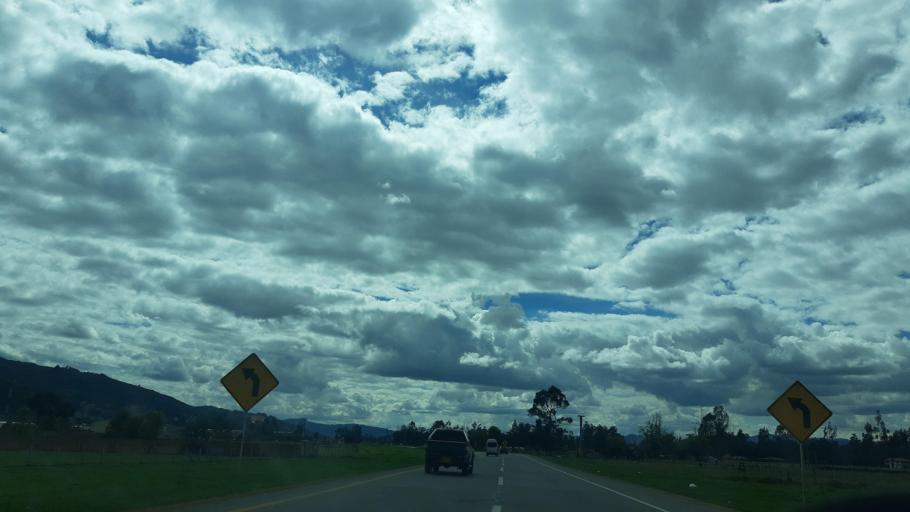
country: CO
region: Cundinamarca
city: Gachancipa
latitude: 4.9989
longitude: -73.8703
